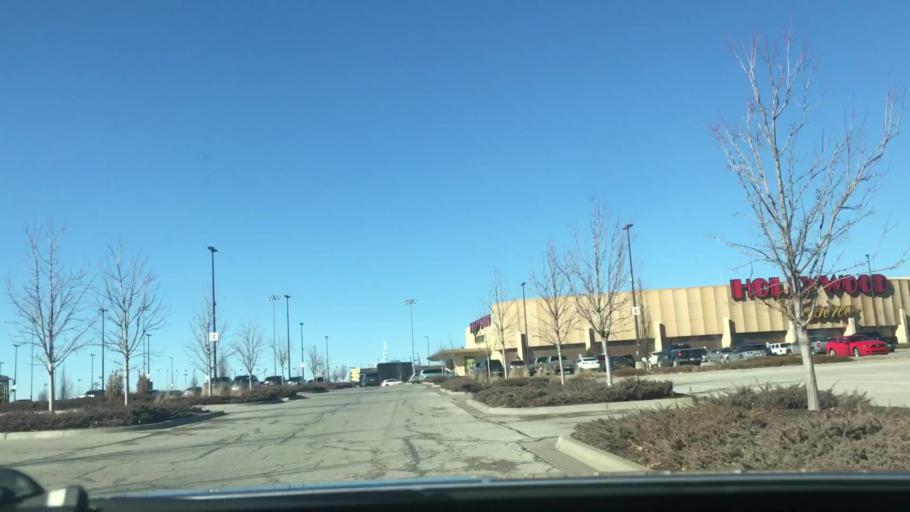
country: US
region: Kansas
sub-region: Wyandotte County
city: Edwardsville
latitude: 39.1101
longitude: -94.8271
